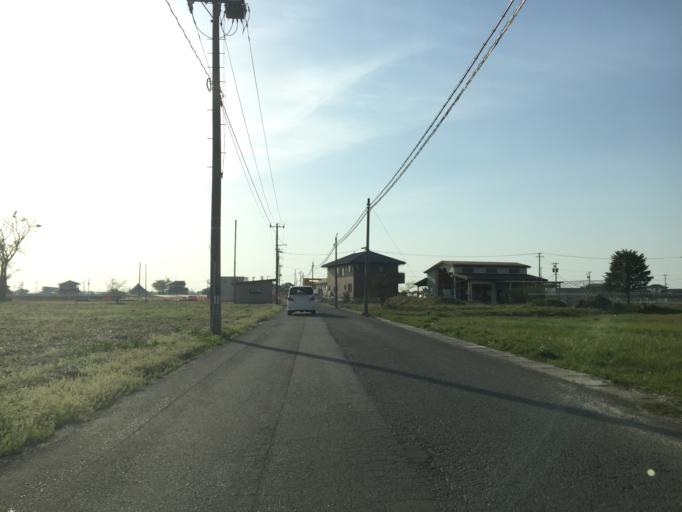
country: JP
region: Miyagi
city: Watari
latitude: 38.0279
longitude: 140.8952
